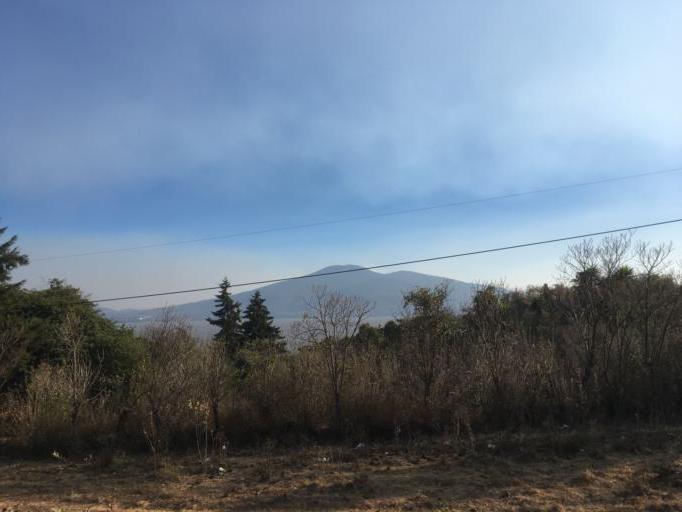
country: MX
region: Michoacan
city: Santa Fe de la Laguna
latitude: 19.6727
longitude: -101.5743
